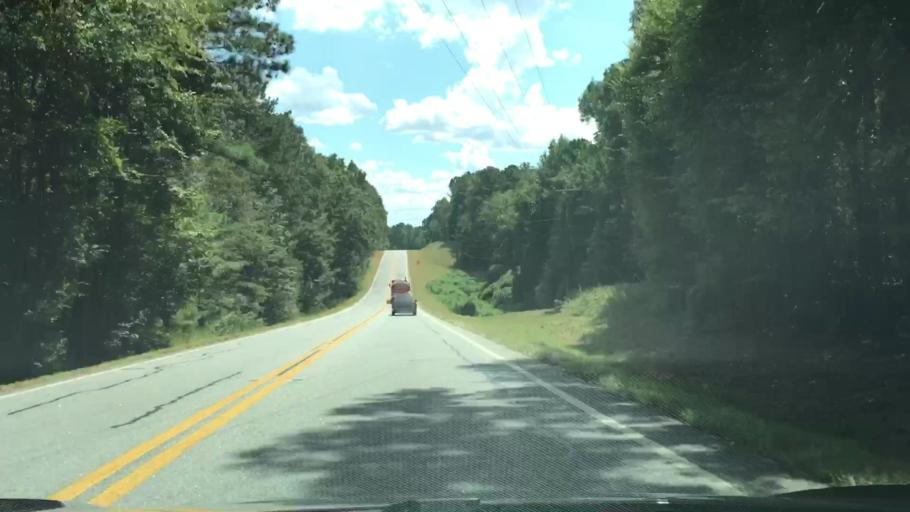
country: US
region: Georgia
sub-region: Oconee County
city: Watkinsville
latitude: 33.7687
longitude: -83.3100
